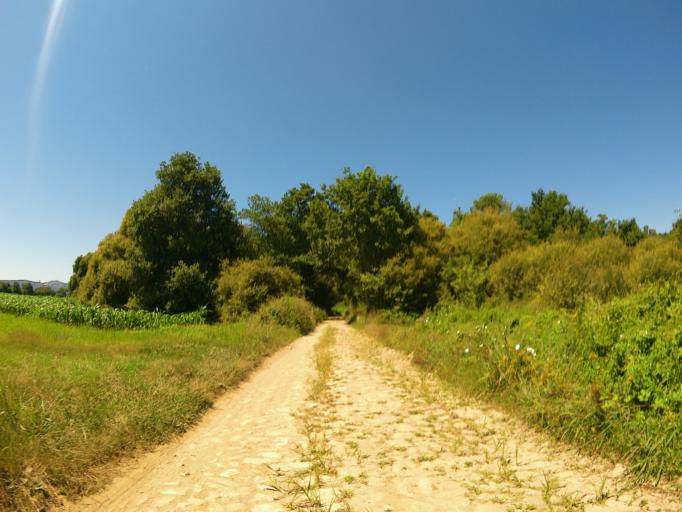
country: PT
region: Viana do Castelo
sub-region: Viana do Castelo
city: Darque
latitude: 41.7222
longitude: -8.7014
